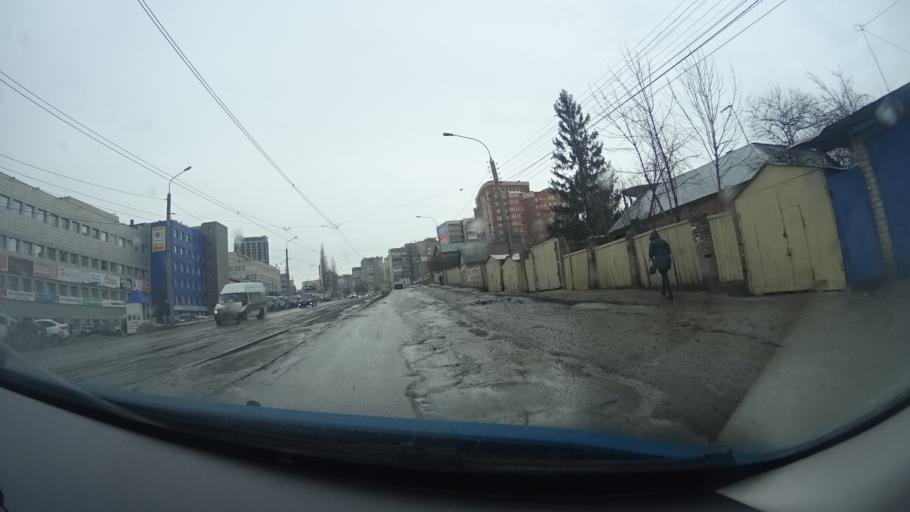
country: RU
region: Bashkortostan
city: Ufa
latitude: 54.7111
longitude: 55.9851
